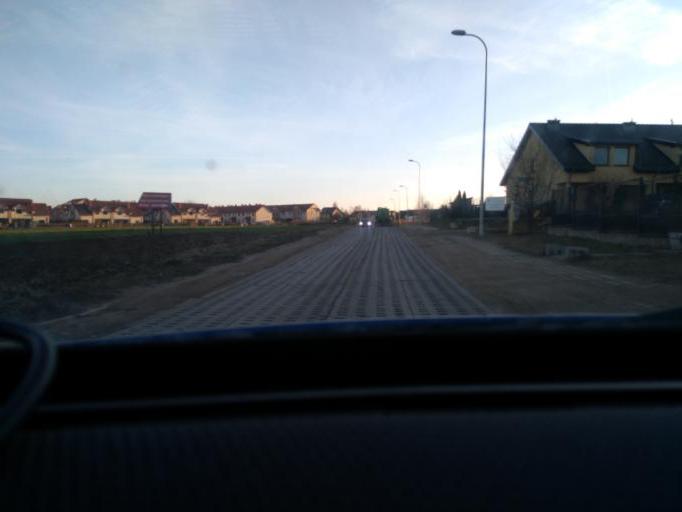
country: PL
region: Pomeranian Voivodeship
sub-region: Powiat kartuski
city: Banino
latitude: 54.3909
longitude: 18.3827
